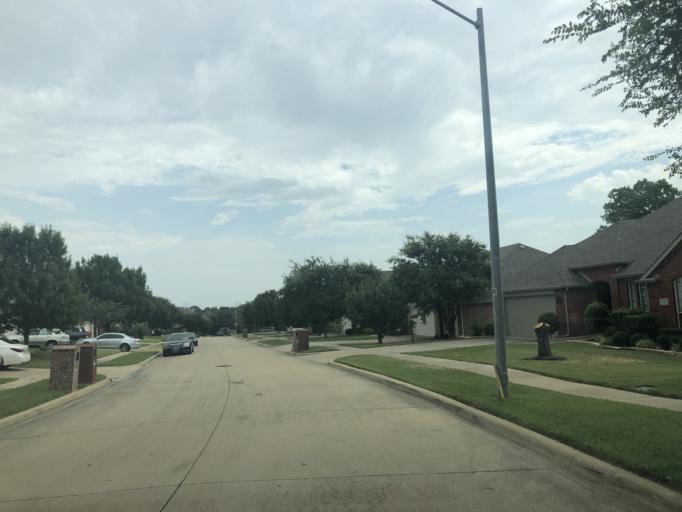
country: US
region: Texas
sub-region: Dallas County
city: Grand Prairie
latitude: 32.7642
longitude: -97.0407
